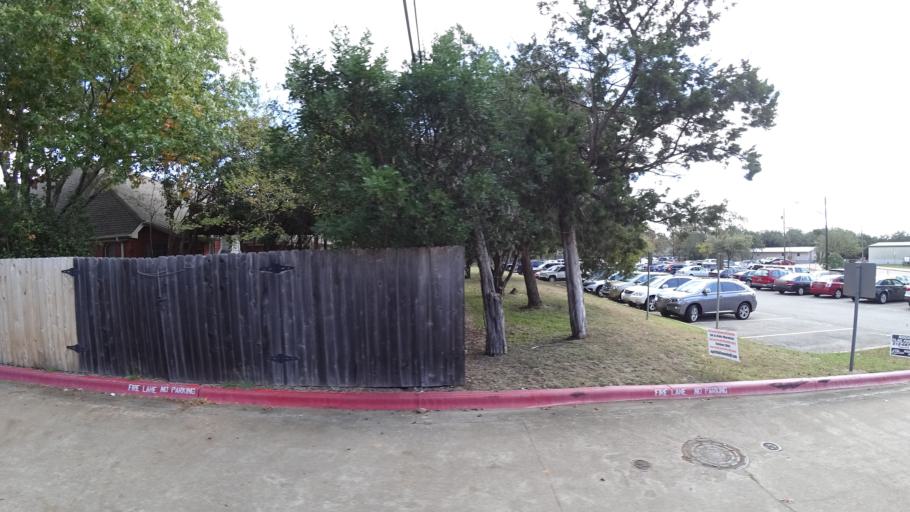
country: US
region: Texas
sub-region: Williamson County
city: Jollyville
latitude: 30.4145
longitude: -97.7806
